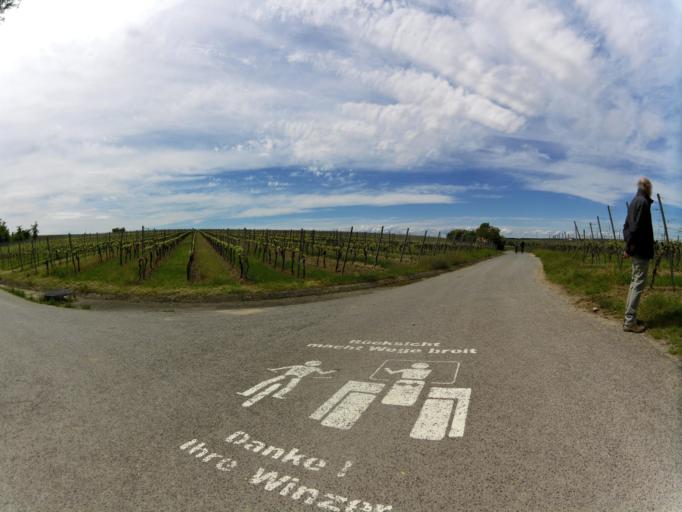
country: DE
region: Bavaria
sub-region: Regierungsbezirk Unterfranken
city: Sommerach
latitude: 49.8503
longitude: 10.2054
